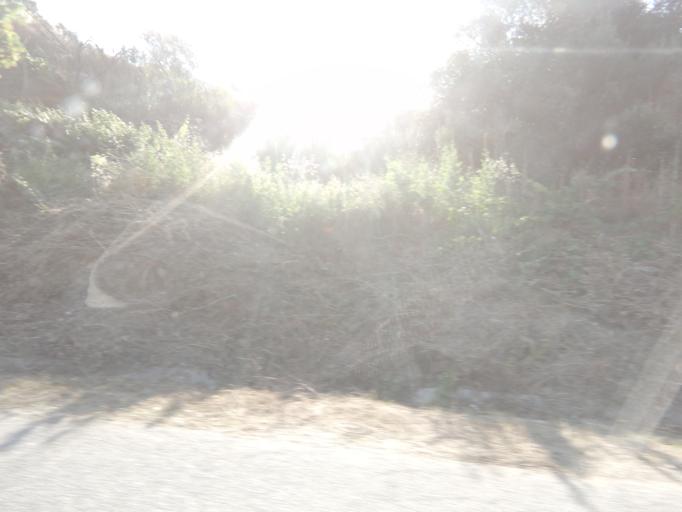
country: PT
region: Vila Real
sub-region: Sabrosa
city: Vilela
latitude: 41.2121
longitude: -7.5546
